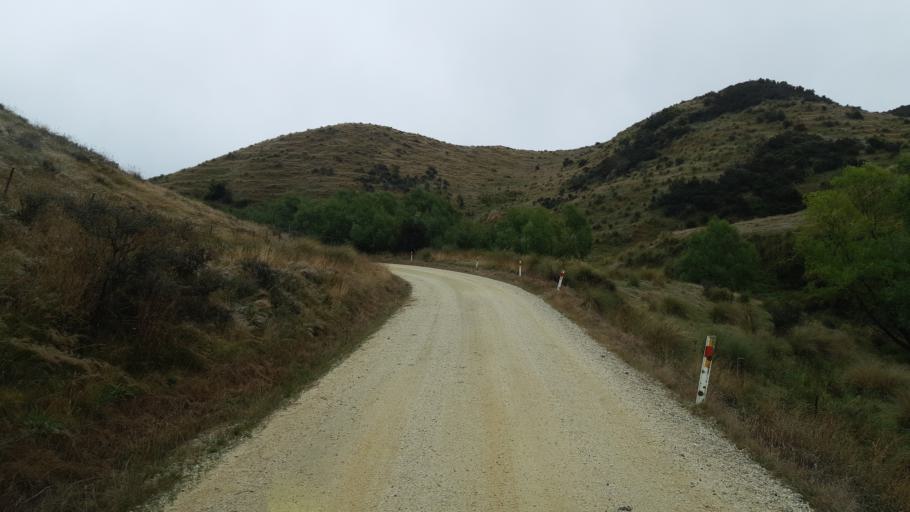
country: NZ
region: Otago
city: Oamaru
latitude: -44.9722
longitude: 170.5034
